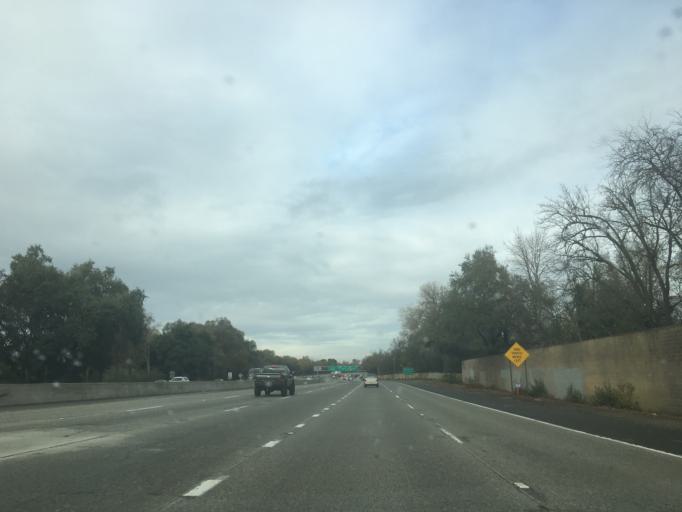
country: US
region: California
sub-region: Yolo County
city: West Sacramento
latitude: 38.5572
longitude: -121.5128
